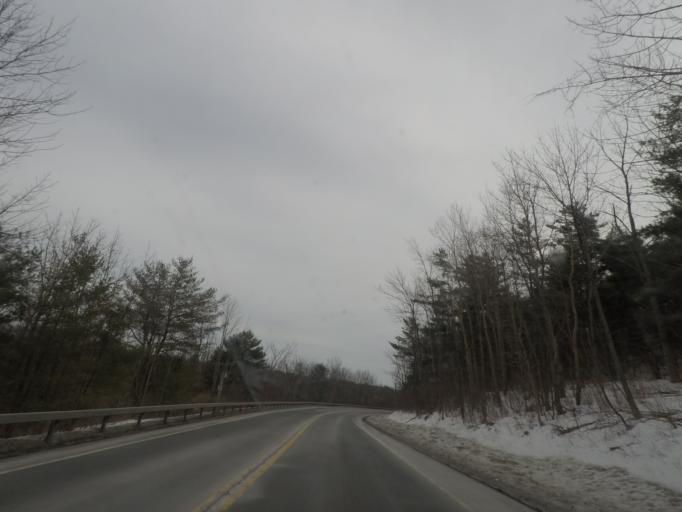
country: US
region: New York
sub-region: Albany County
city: Voorheesville
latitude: 42.5968
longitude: -73.9896
